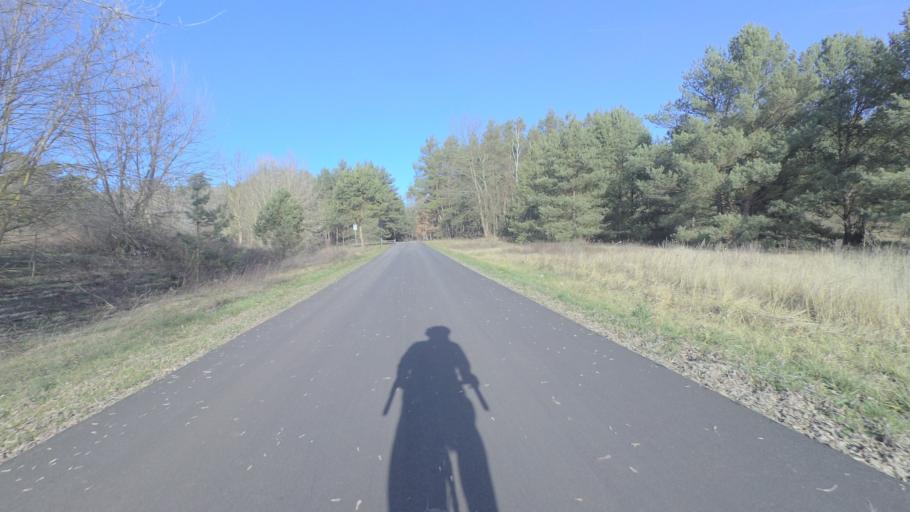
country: DE
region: Brandenburg
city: Luckenwalde
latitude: 52.0462
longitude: 13.1406
